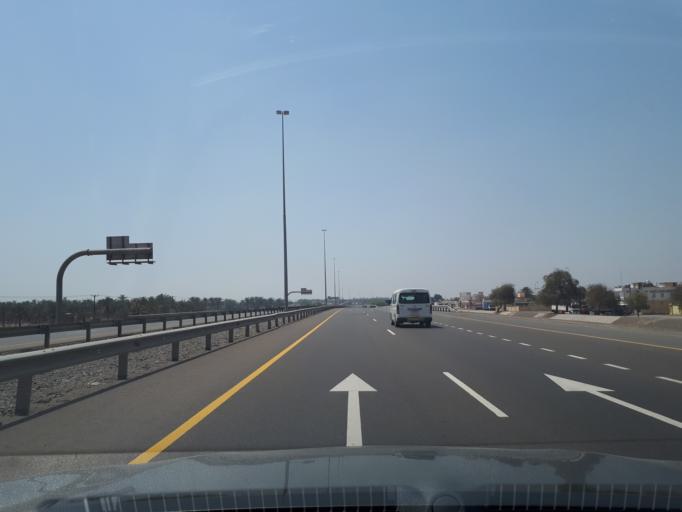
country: OM
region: Al Batinah
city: Al Liwa'
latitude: 24.5015
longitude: 56.5692
